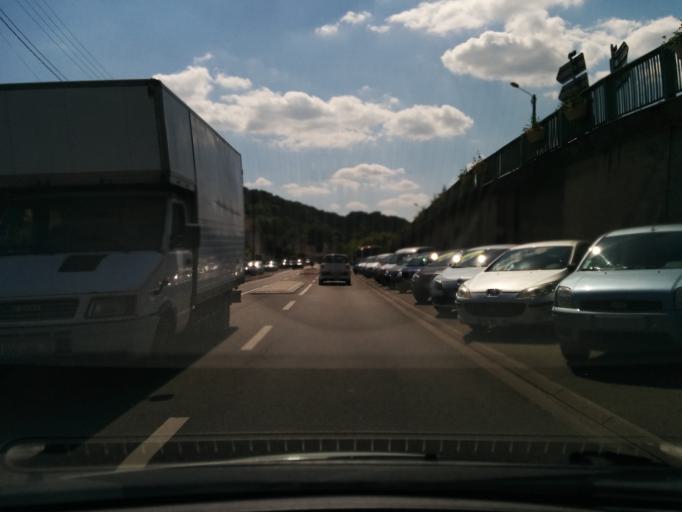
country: FR
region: Ile-de-France
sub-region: Departement des Yvelines
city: Bonnieres-sur-Seine
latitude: 49.0355
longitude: 1.5739
